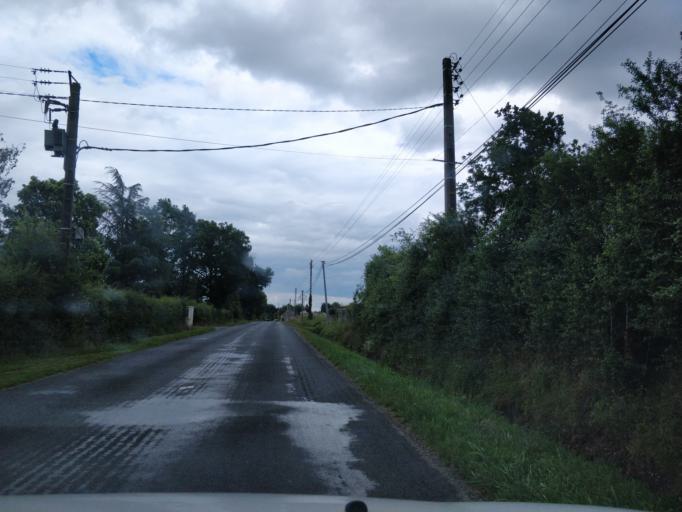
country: FR
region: Pays de la Loire
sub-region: Departement de Maine-et-Loire
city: Grez-Neuville
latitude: 47.6388
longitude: -0.6486
